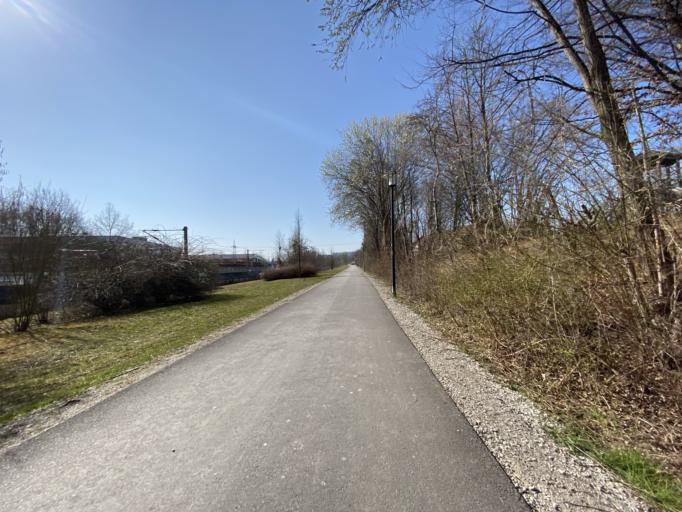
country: DE
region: Bavaria
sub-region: Upper Bavaria
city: Unterfoehring
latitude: 48.1876
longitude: 11.6451
